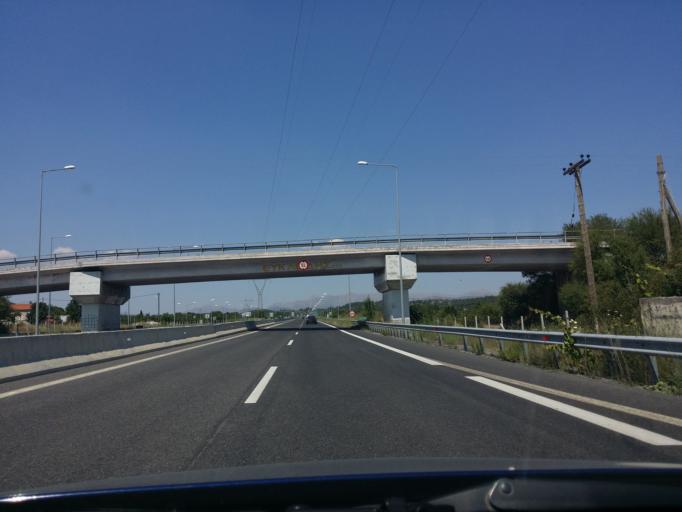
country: GR
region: Peloponnese
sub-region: Nomos Arkadias
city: Tripoli
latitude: 37.4658
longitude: 22.3306
